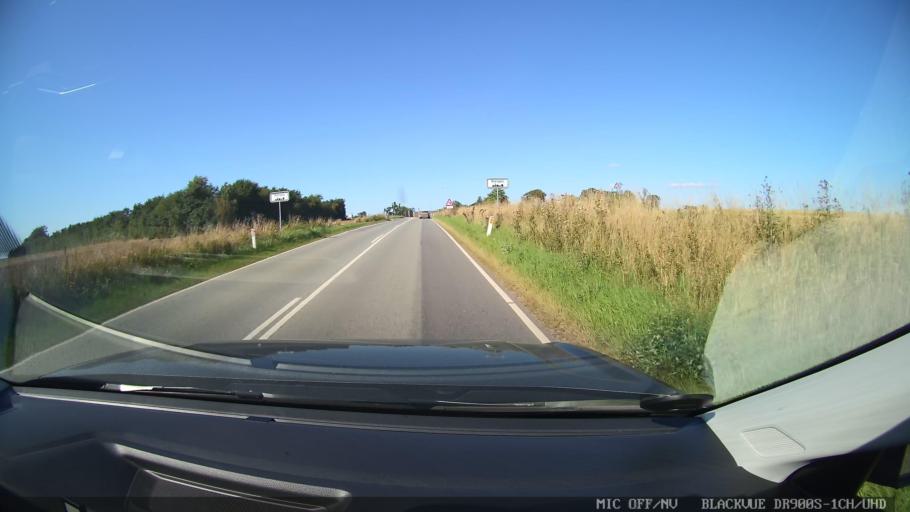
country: DK
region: Central Jutland
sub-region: Randers Kommune
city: Spentrup
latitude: 56.5210
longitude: 10.0097
